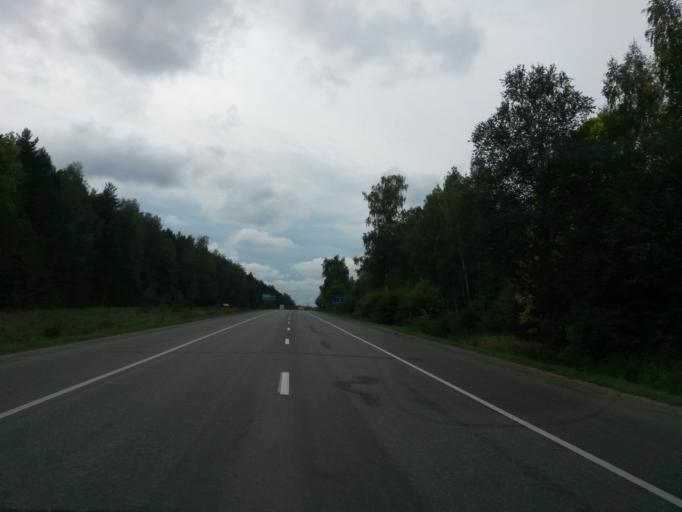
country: RU
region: Moskovskaya
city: Stolbovaya
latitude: 55.1963
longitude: 37.5049
